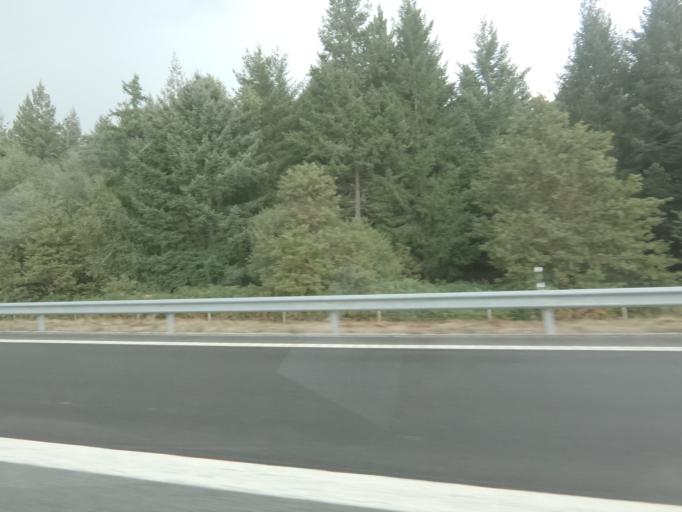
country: PT
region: Viseu
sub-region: Viseu
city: Abraveses
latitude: 40.6894
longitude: -7.9658
